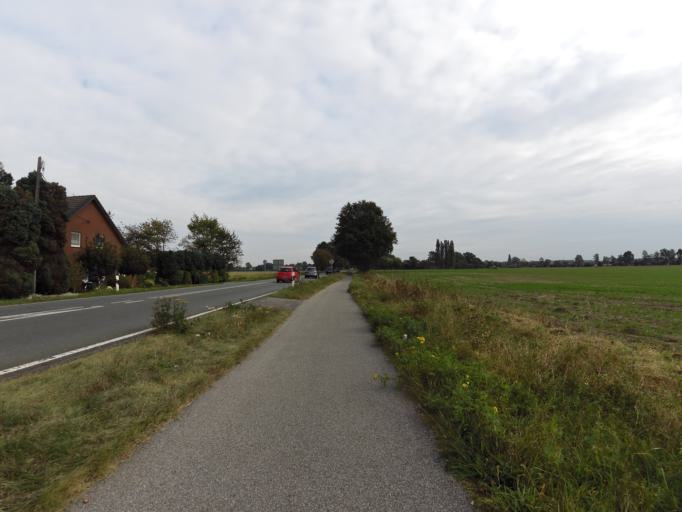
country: DE
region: North Rhine-Westphalia
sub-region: Regierungsbezirk Dusseldorf
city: Bocholt
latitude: 51.8336
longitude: 6.5584
